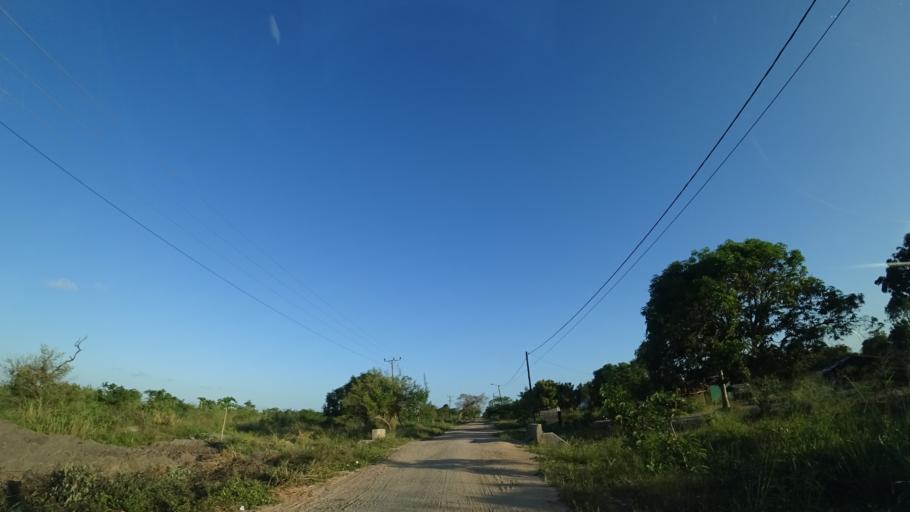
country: MZ
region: Sofala
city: Dondo
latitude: -19.3935
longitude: 34.7087
